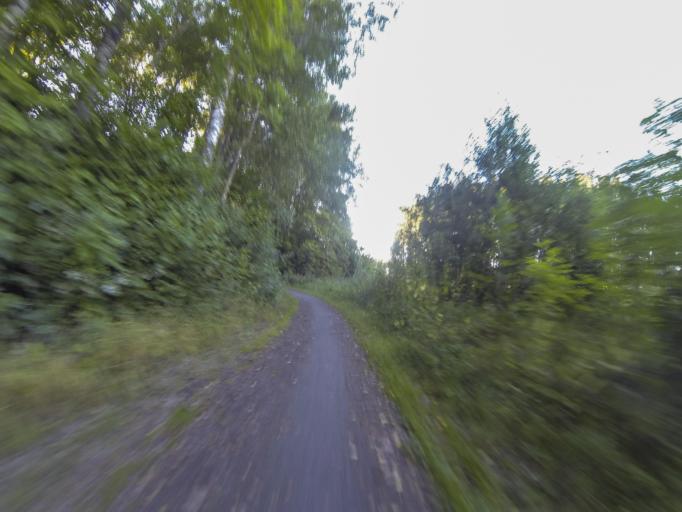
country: SE
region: Vaestmanland
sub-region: Vasteras
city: Vasteras
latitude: 59.5722
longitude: 16.6402
